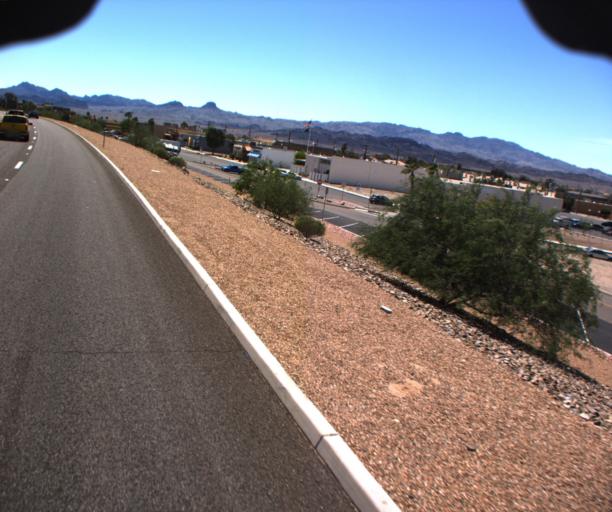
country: US
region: Arizona
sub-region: Mohave County
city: Lake Havasu City
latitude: 34.4775
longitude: -114.3488
